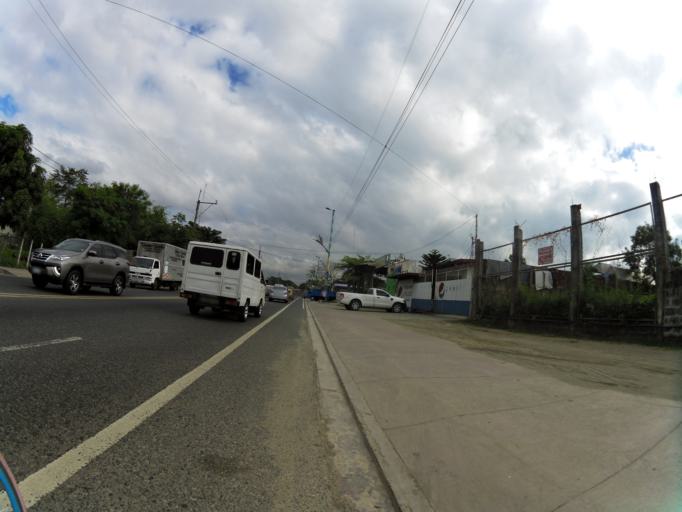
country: PH
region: Metro Manila
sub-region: Marikina
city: Calumpang
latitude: 14.6390
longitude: 121.1028
